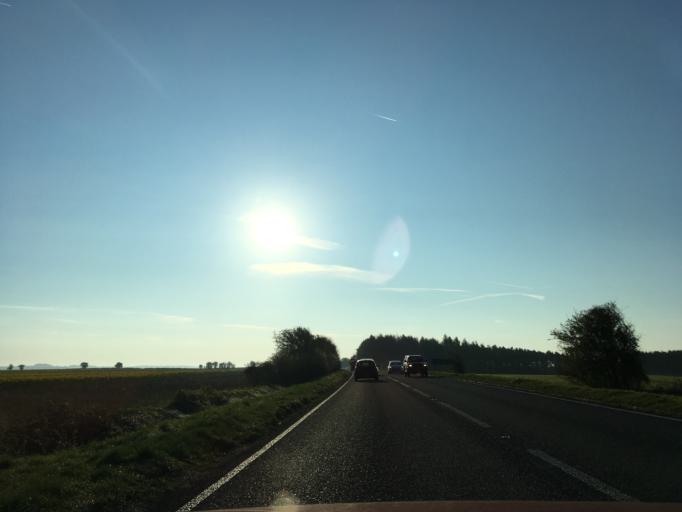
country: GB
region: England
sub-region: Gloucestershire
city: Bourton on the Water
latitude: 51.8155
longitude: -1.7479
